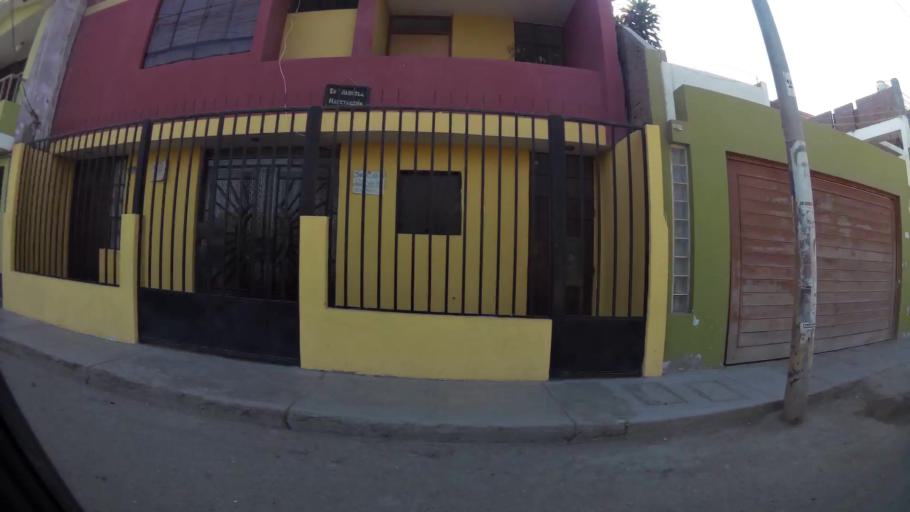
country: PE
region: Lambayeque
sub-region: Provincia de Chiclayo
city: Chiclayo
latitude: -6.7642
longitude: -79.8458
